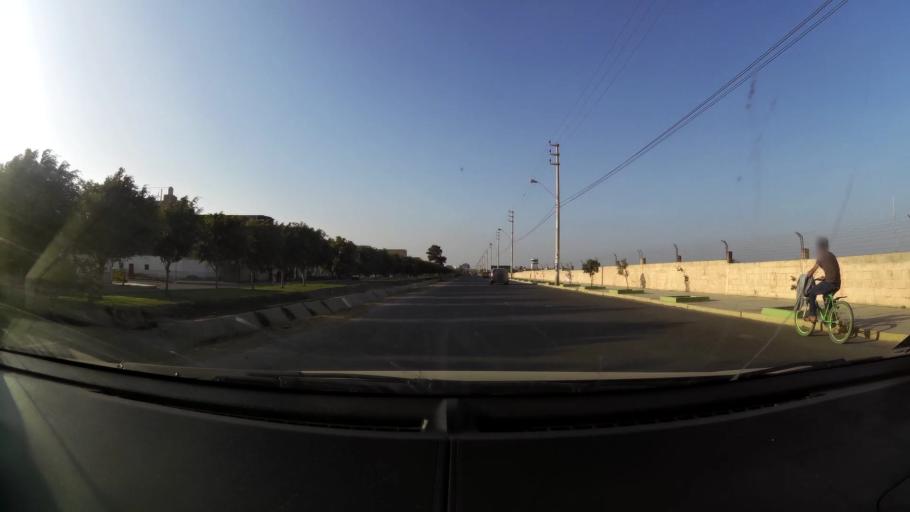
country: PE
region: Lambayeque
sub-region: Provincia de Chiclayo
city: Chiclayo
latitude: -6.7817
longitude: -79.8312
